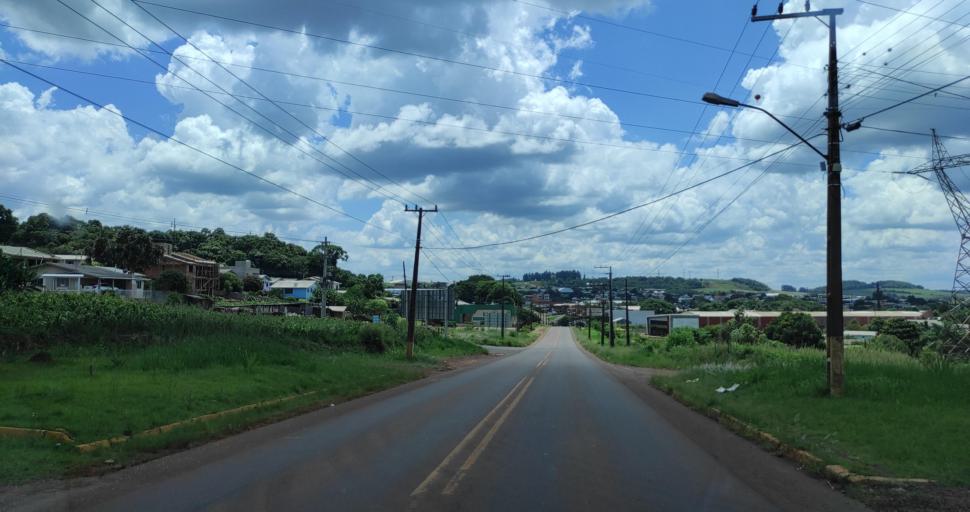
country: BR
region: Santa Catarina
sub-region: Xanxere
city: Xanxere
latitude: -26.8654
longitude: -52.4090
